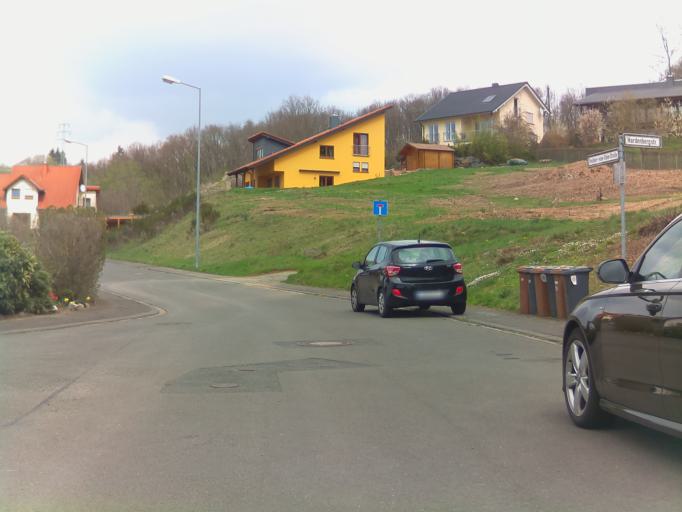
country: DE
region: Rheinland-Pfalz
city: Kirn
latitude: 49.7999
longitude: 7.4668
